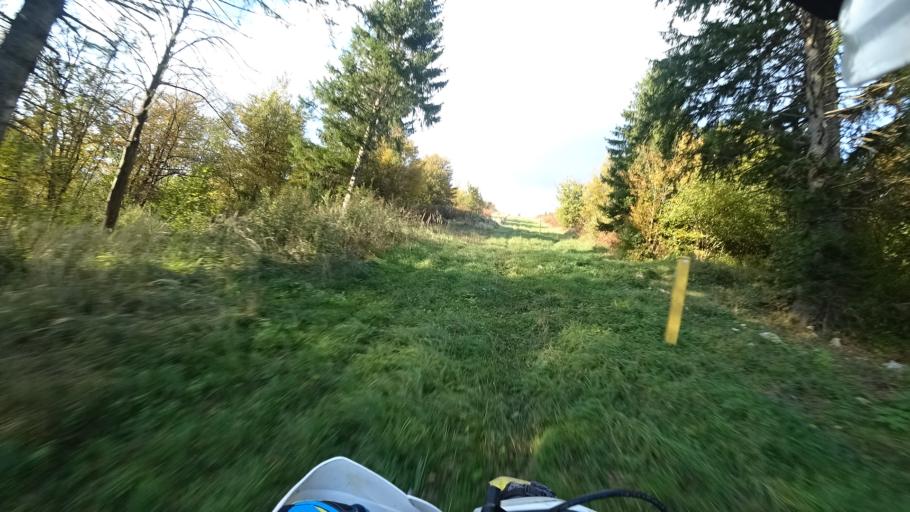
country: HR
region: Karlovacka
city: Plaski
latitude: 45.0118
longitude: 15.4221
